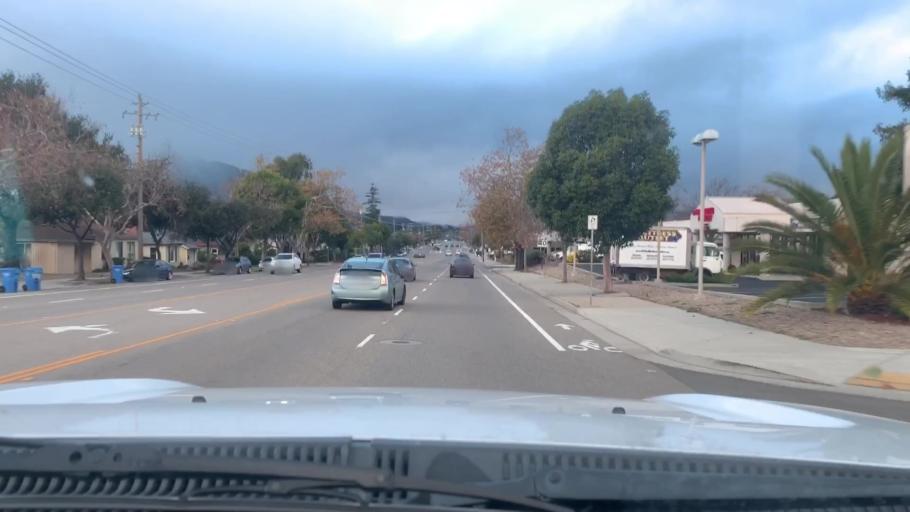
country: US
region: California
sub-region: San Luis Obispo County
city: San Luis Obispo
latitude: 35.2658
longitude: -120.6533
